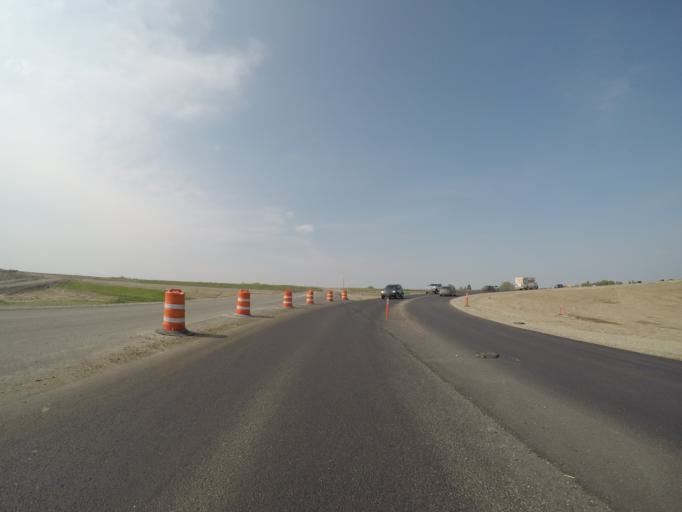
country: US
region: Montana
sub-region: Yellowstone County
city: Laurel
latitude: 45.6397
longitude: -108.7666
